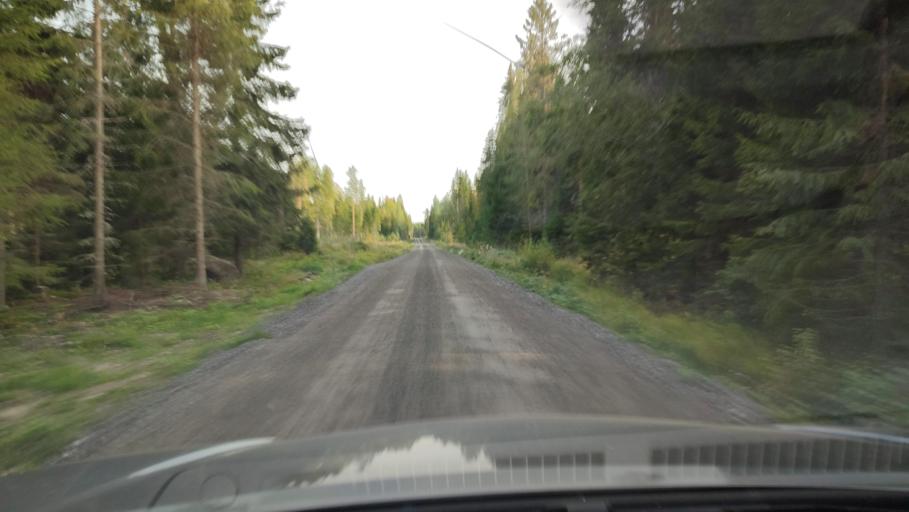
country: FI
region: Southern Ostrobothnia
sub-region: Suupohja
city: Karijoki
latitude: 62.1654
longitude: 21.6078
